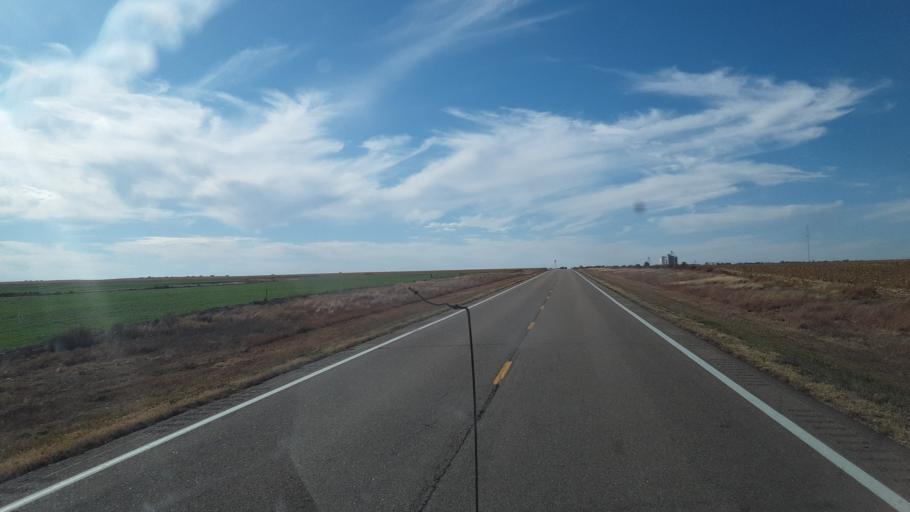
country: US
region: Kansas
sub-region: Edwards County
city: Kinsley
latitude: 38.1896
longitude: -99.4974
